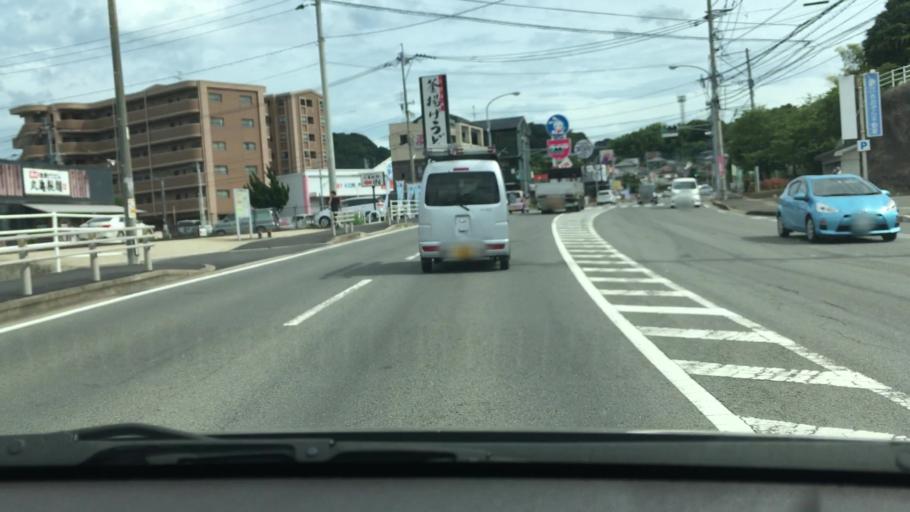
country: JP
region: Nagasaki
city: Togitsu
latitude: 32.8397
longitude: 129.8377
